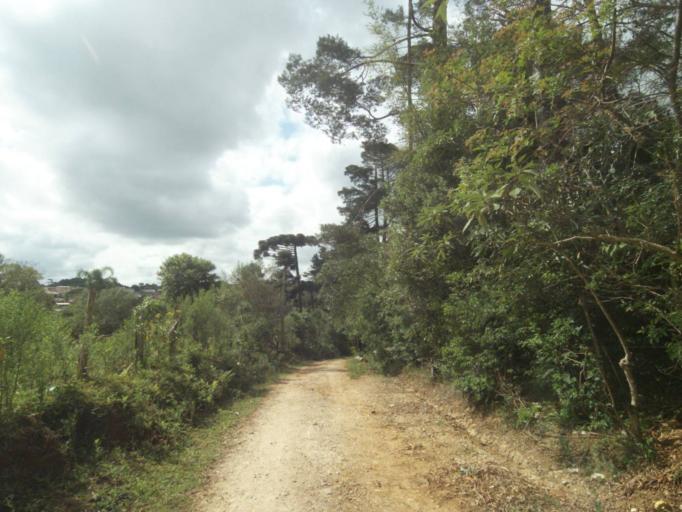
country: BR
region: Parana
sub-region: Almirante Tamandare
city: Almirante Tamandare
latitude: -25.3768
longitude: -49.2945
